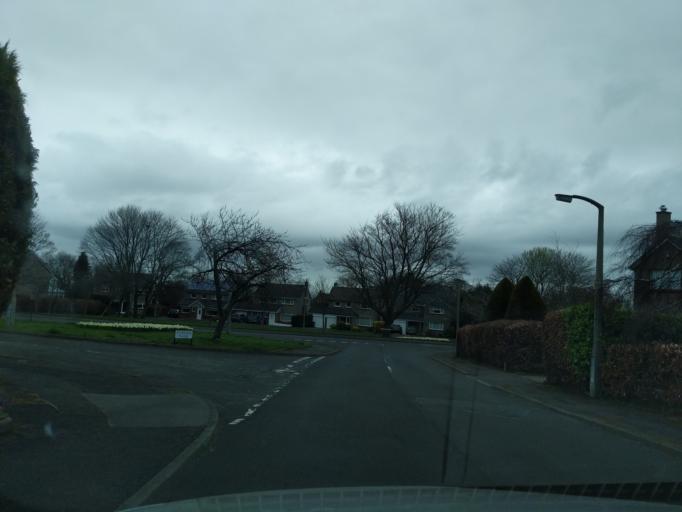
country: GB
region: Scotland
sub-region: Edinburgh
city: Balerno
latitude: 55.8899
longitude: -3.3434
